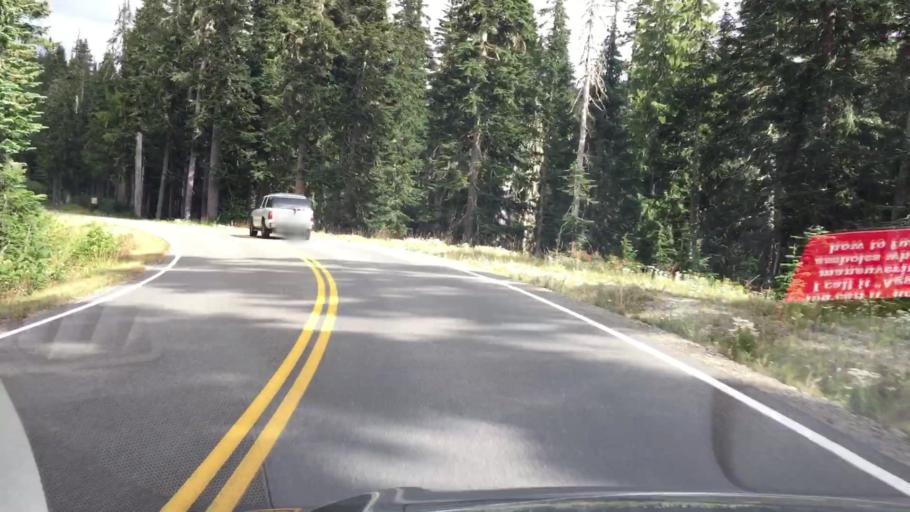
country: US
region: Washington
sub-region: Pierce County
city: Buckley
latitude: 46.7693
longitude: -121.7425
